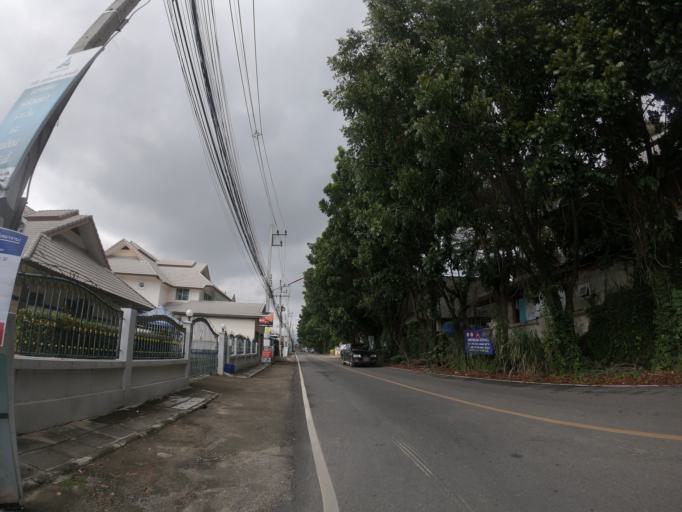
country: TH
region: Chiang Mai
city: Chiang Mai
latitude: 18.7492
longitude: 98.9794
